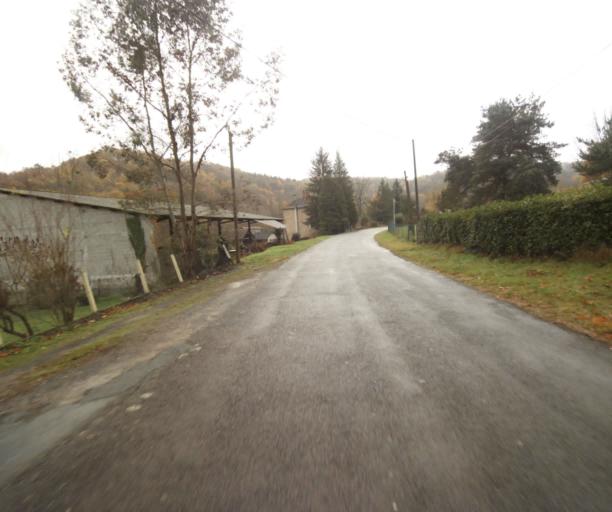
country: FR
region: Limousin
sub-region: Departement de la Correze
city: Cornil
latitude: 45.1830
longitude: 1.6574
